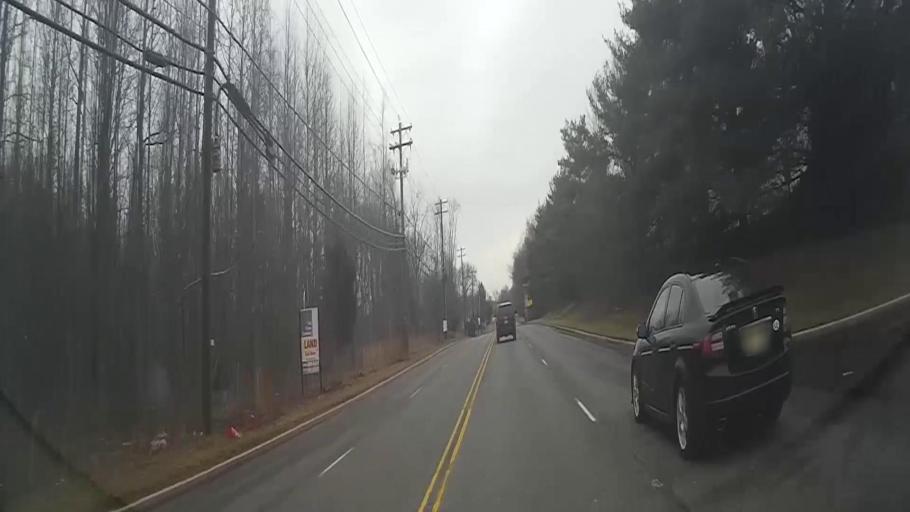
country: US
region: New Jersey
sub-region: Burlington County
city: Marlton
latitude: 39.8733
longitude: -74.9287
